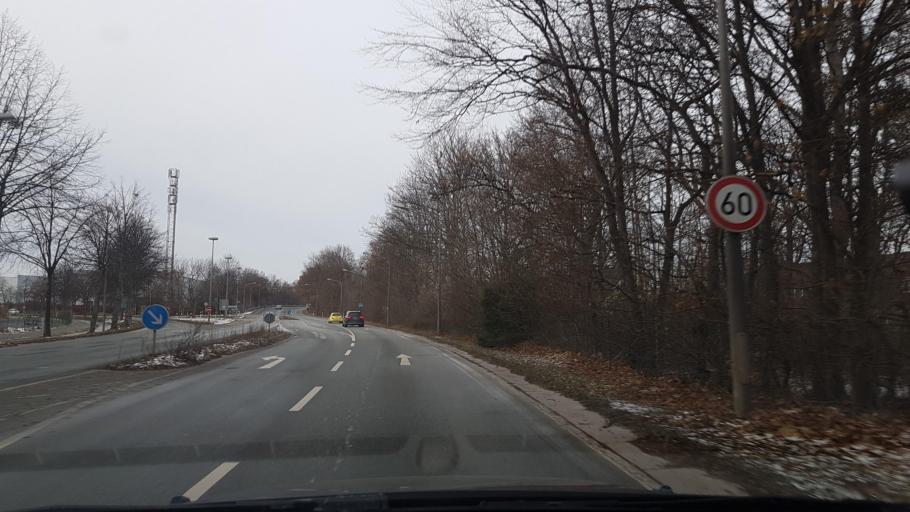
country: DE
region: Lower Saxony
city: Goslar
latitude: 51.9144
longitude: 10.4572
